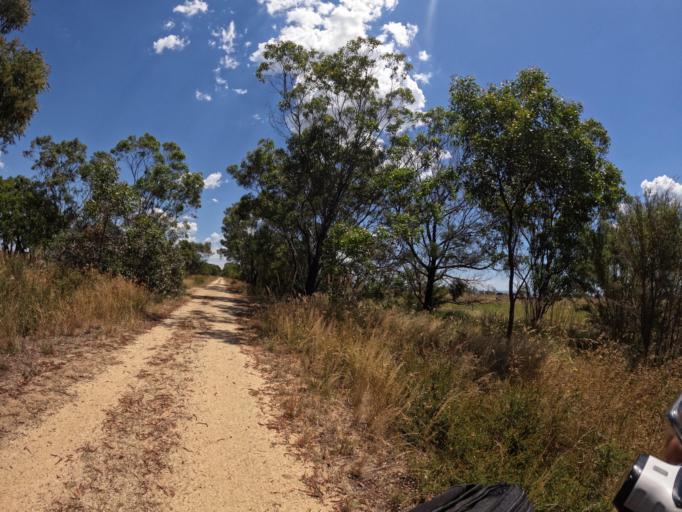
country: AU
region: Victoria
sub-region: Wellington
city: Heyfield
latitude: -37.9785
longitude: 146.8522
